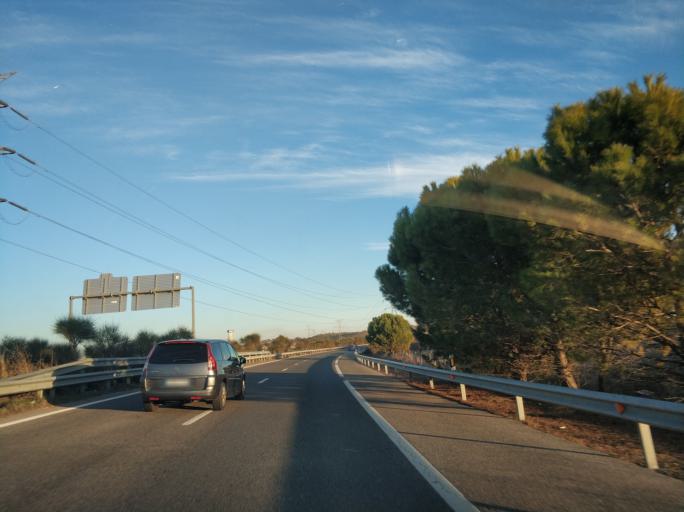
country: ES
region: Madrid
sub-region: Provincia de Madrid
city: Valdemoro
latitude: 40.2206
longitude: -3.6701
